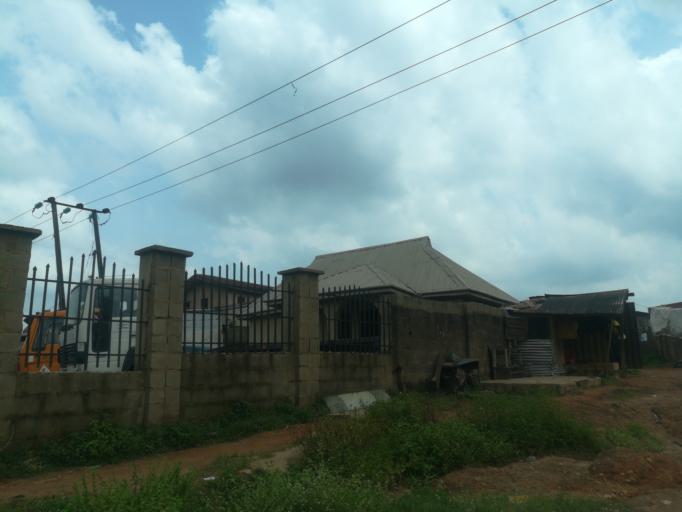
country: NG
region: Oyo
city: Ibadan
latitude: 7.4172
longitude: 3.9421
